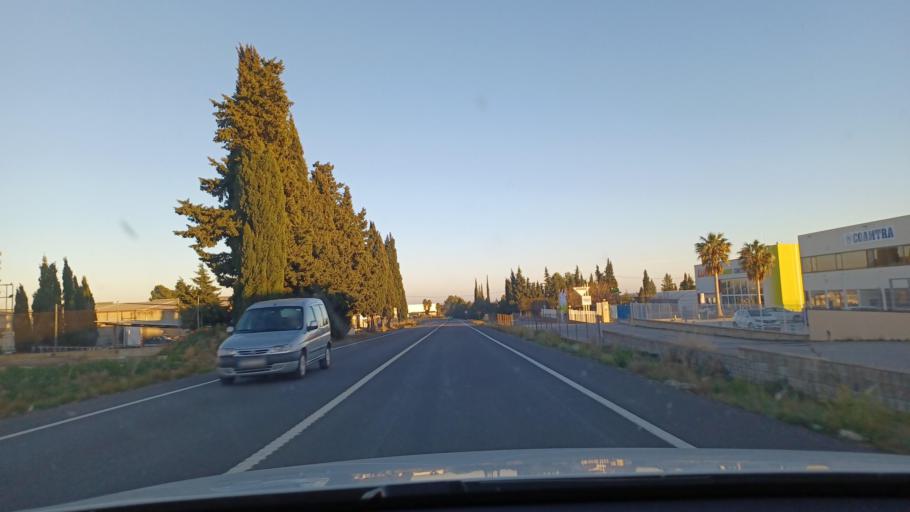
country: ES
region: Catalonia
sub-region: Provincia de Tarragona
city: Amposta
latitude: 40.6975
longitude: 0.5732
